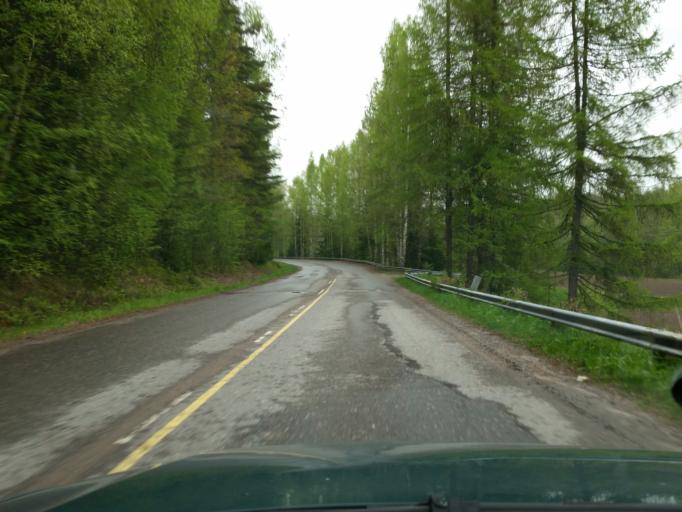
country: FI
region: Uusimaa
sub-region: Helsinki
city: Karjalohja
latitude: 60.1421
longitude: 23.8493
